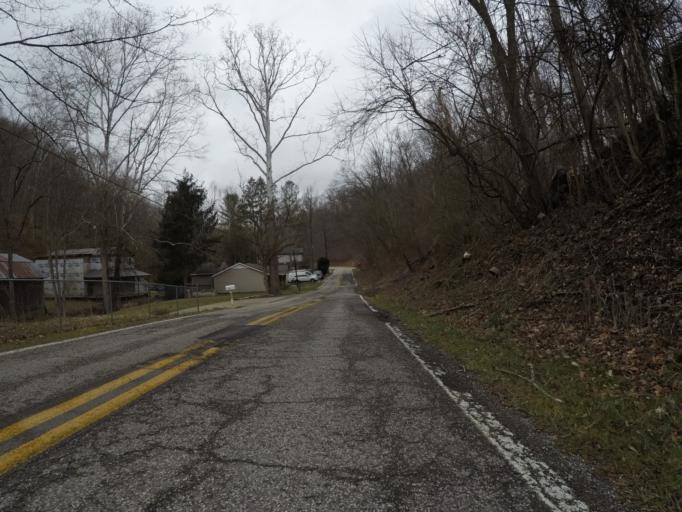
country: US
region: West Virginia
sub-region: Cabell County
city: Barboursville
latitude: 38.4492
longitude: -82.2578
